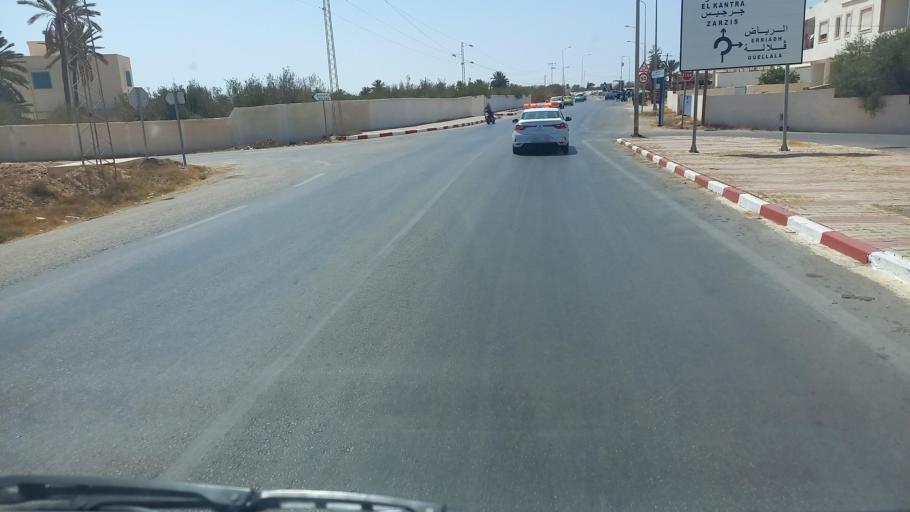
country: TN
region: Madanin
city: Houmt Souk
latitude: 33.8249
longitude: 10.8705
